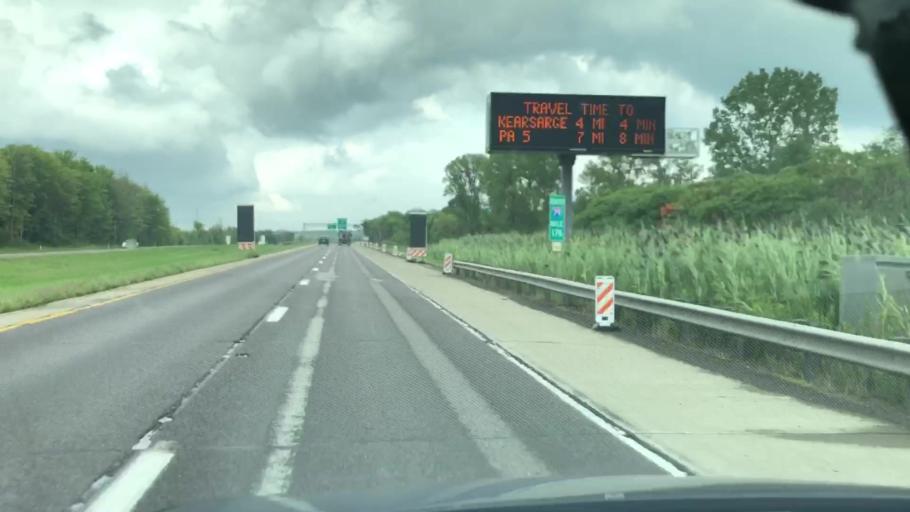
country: US
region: Pennsylvania
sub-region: Erie County
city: Fairview
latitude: 42.0176
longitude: -80.1379
